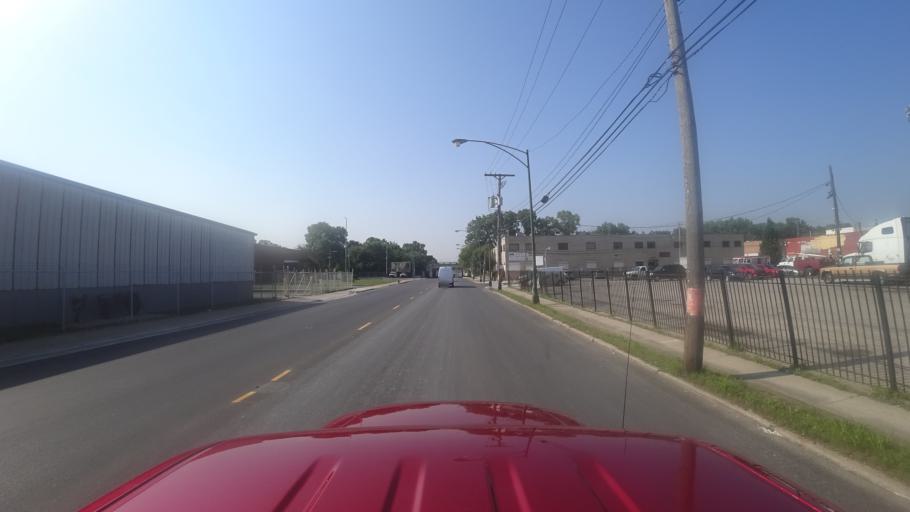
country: US
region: Illinois
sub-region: Cook County
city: Chicago
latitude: 41.8061
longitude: -87.6942
